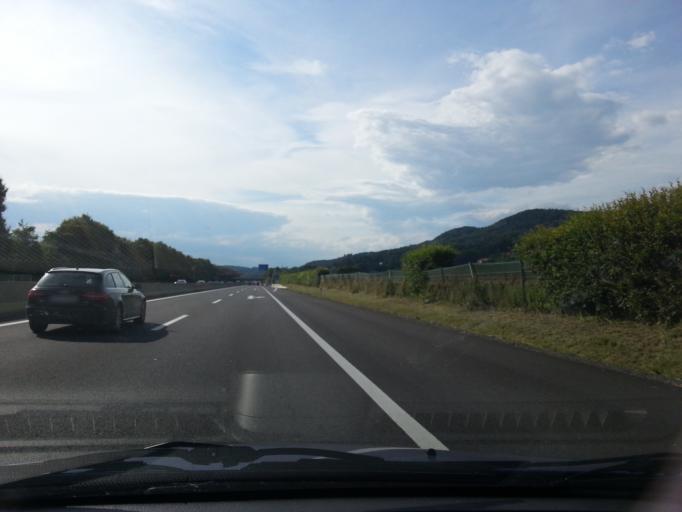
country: AT
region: Styria
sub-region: Politischer Bezirk Leibnitz
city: Lang
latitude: 46.8494
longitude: 15.5215
